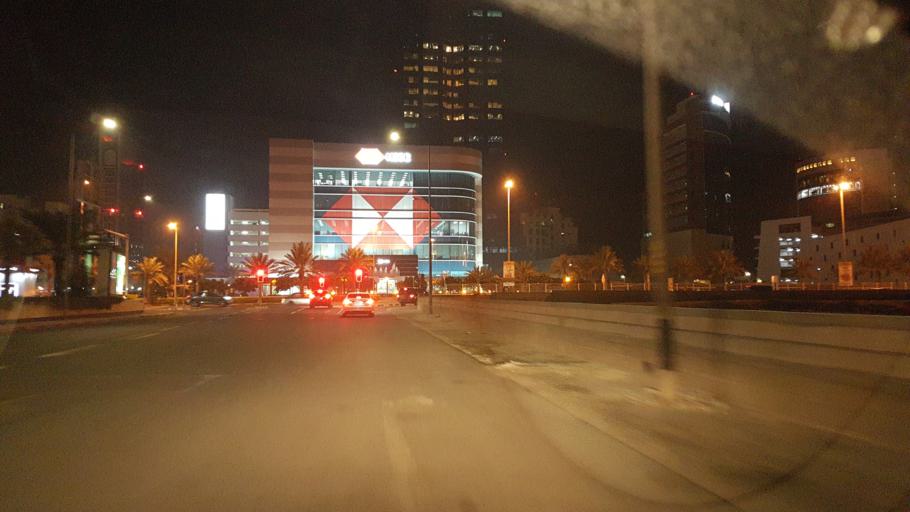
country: BH
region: Manama
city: Jidd Hafs
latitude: 26.2338
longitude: 50.5416
